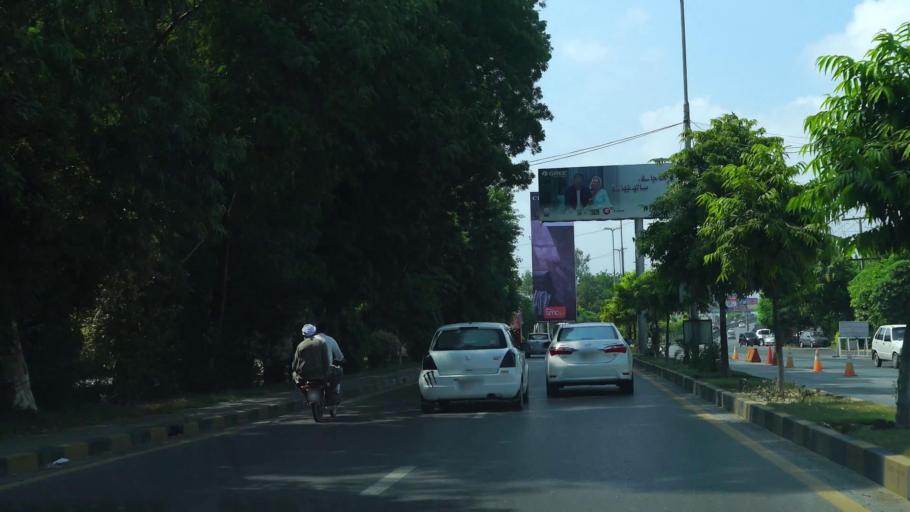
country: PK
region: Punjab
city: Lahore
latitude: 31.5263
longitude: 74.3628
